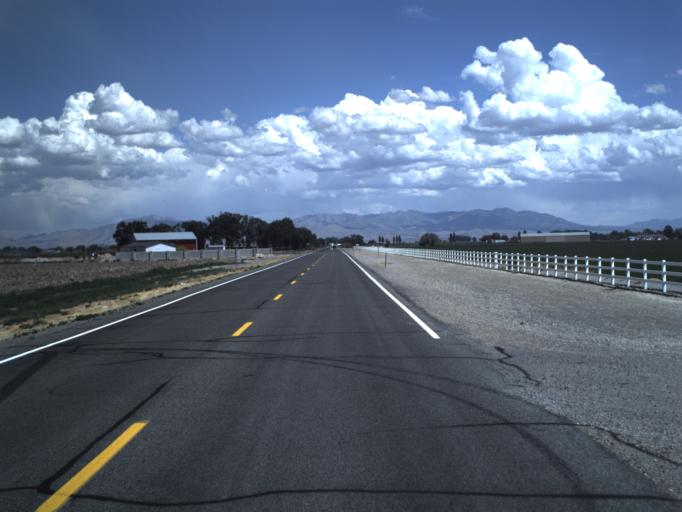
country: US
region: Utah
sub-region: Millard County
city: Delta
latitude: 39.3306
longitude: -112.6336
